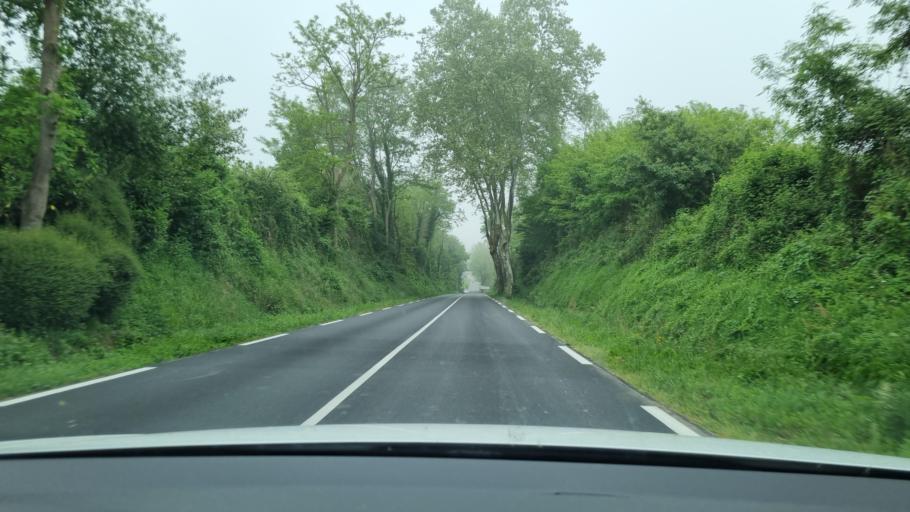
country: FR
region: Aquitaine
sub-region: Departement des Landes
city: Amou
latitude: 43.5376
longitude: -0.6878
